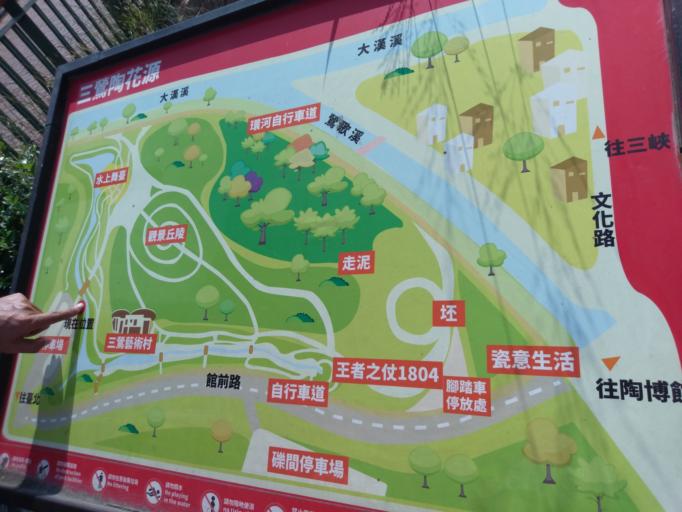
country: TW
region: Taiwan
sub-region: Taoyuan
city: Taoyuan
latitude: 24.9539
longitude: 121.3593
